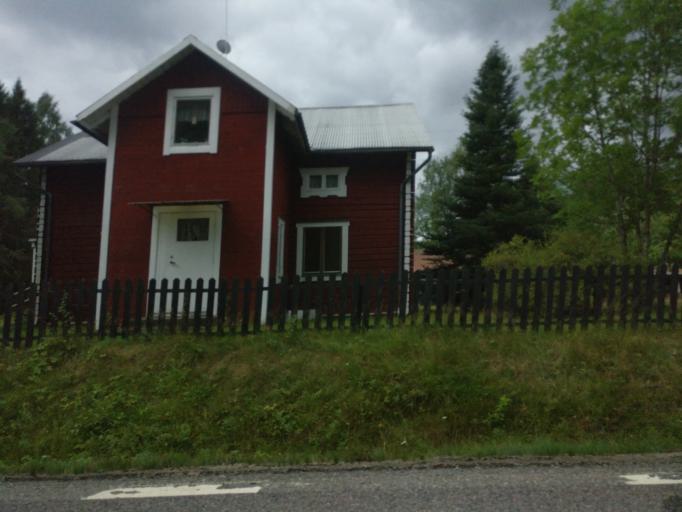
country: SE
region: Vaermland
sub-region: Torsby Kommun
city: Torsby
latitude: 60.7705
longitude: 12.7555
